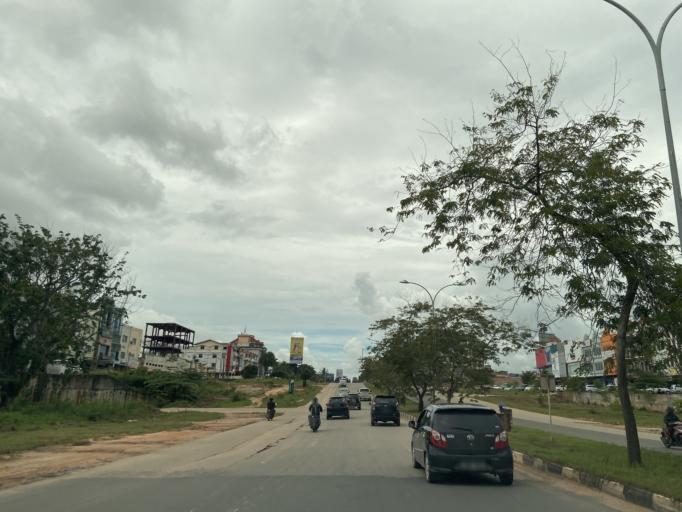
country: SG
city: Singapore
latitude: 1.1294
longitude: 104.0303
